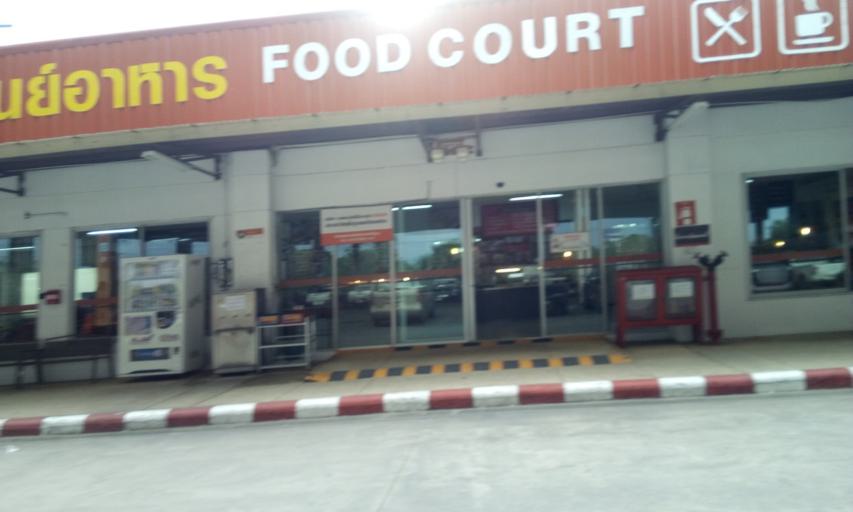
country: TH
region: Pathum Thani
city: Ban Rangsit
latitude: 14.0277
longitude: 100.7498
